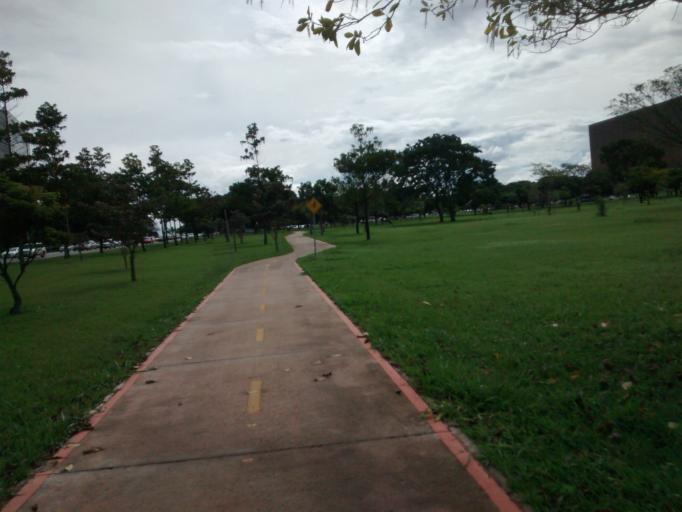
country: BR
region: Federal District
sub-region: Brasilia
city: Brasilia
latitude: -15.7875
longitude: -47.9060
